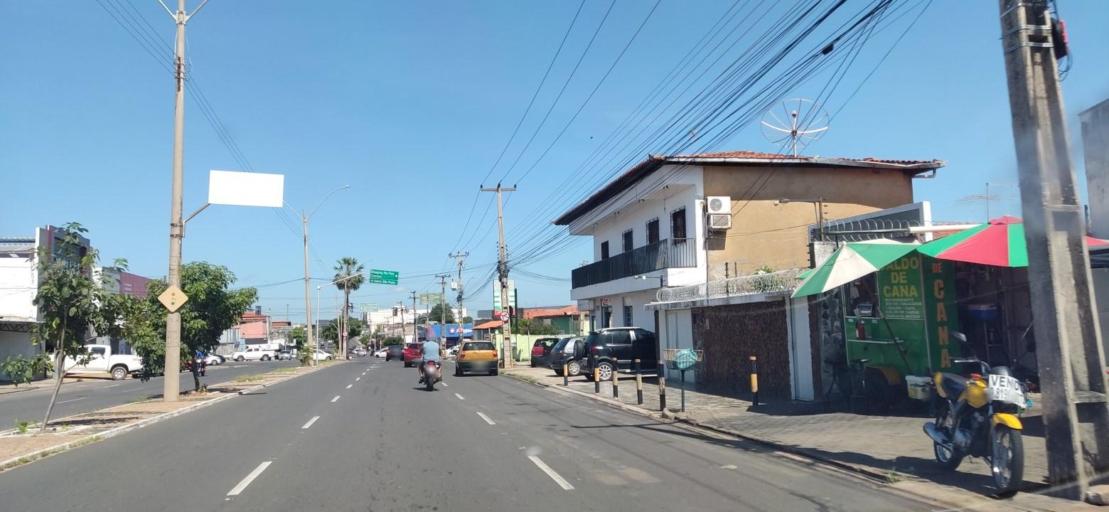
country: BR
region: Piaui
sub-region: Teresina
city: Teresina
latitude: -5.1120
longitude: -42.8011
